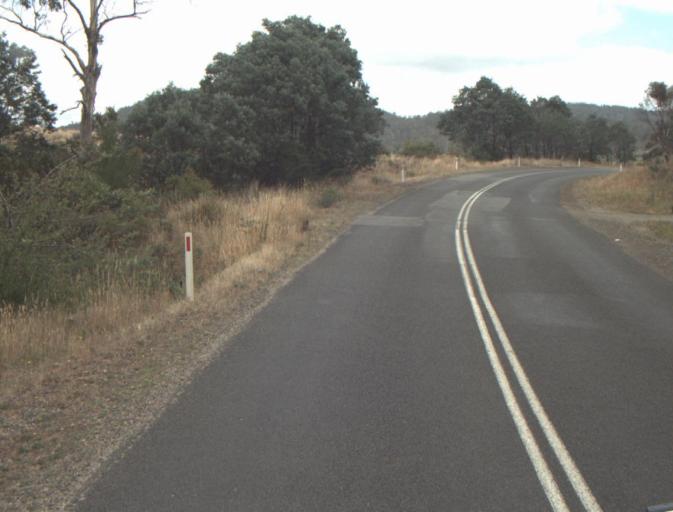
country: AU
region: Tasmania
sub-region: Northern Midlands
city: Evandale
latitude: -41.5058
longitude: 147.3807
